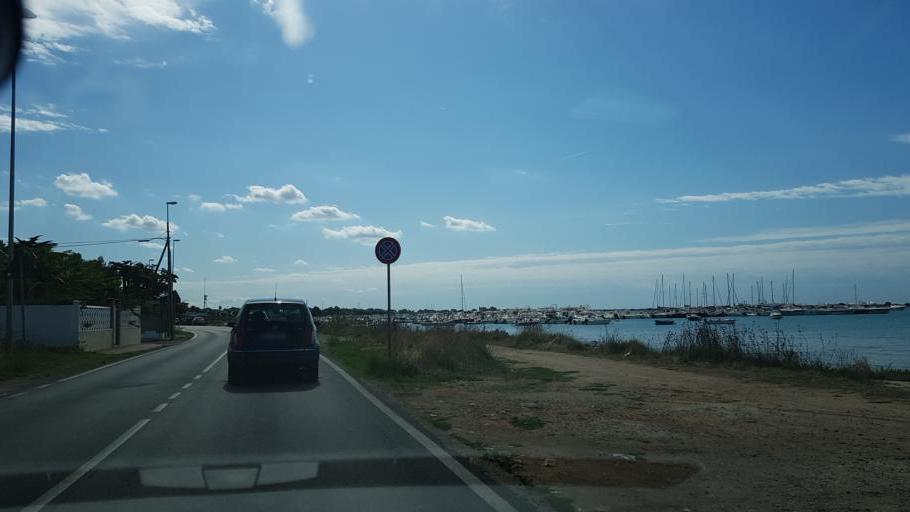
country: IT
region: Apulia
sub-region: Provincia di Lecce
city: Porto Cesareo
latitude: 40.2554
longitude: 17.9053
